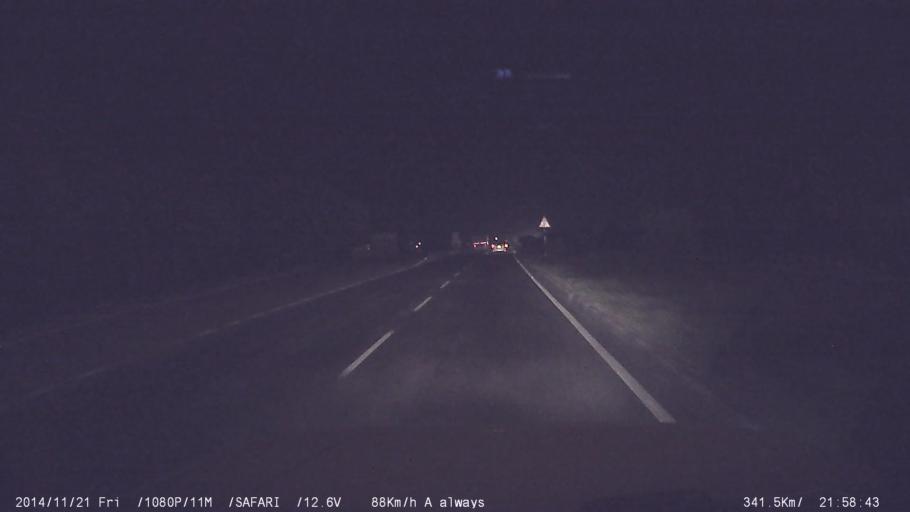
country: IN
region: Tamil Nadu
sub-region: Kancheepuram
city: Madurantakam
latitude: 12.5843
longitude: 79.9194
